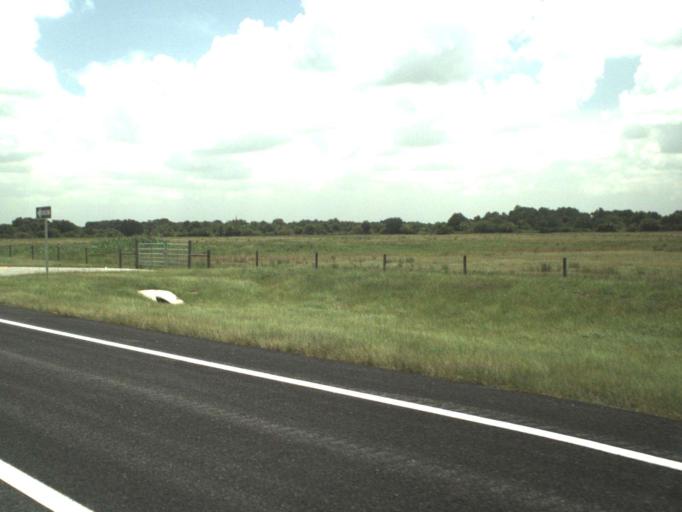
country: US
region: Florida
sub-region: Okeechobee County
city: Cypress Quarters
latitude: 27.3528
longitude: -80.6333
